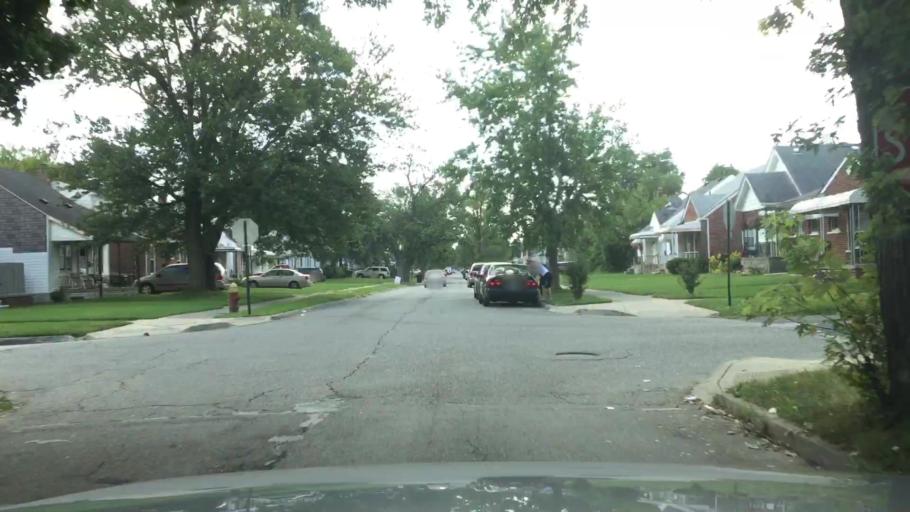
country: US
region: Michigan
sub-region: Wayne County
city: Dearborn Heights
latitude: 42.3398
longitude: -83.2242
